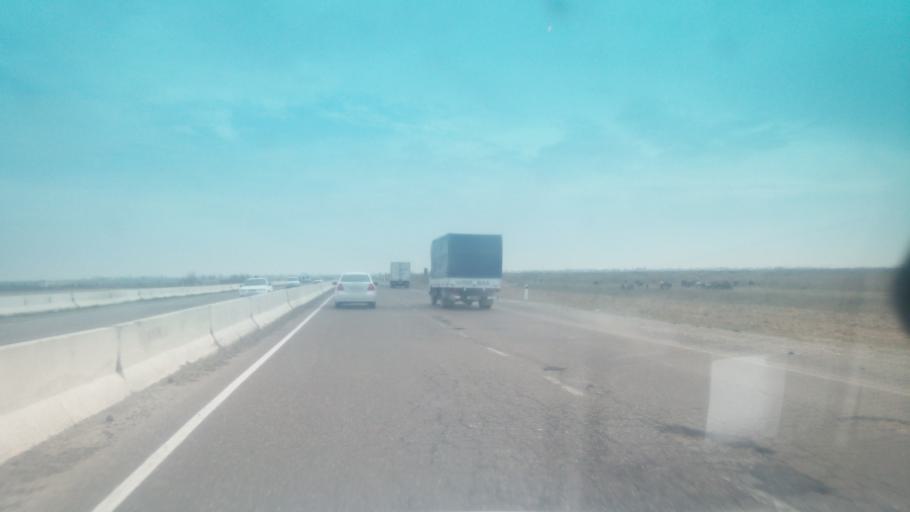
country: KZ
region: Ongtustik Qazaqstan
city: Myrzakent
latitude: 40.5127
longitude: 68.4914
